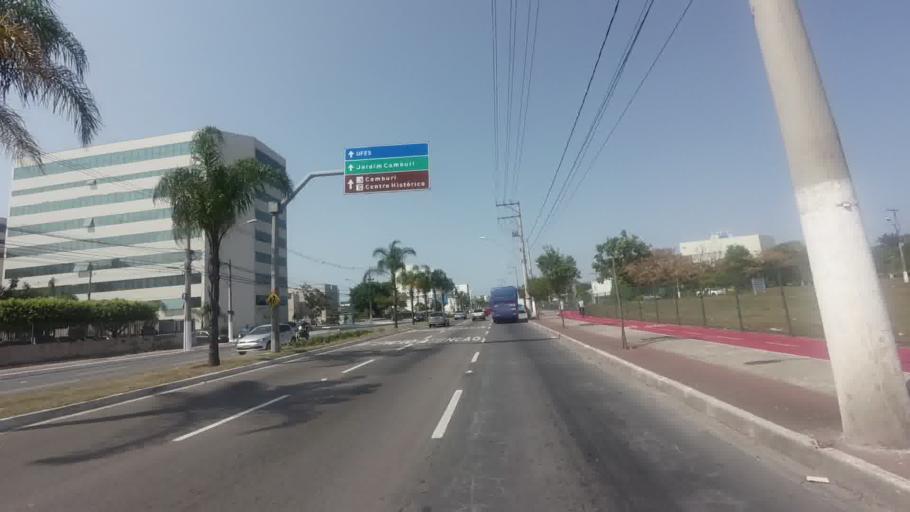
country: BR
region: Espirito Santo
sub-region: Vila Velha
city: Vila Velha
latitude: -20.2759
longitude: -40.3009
